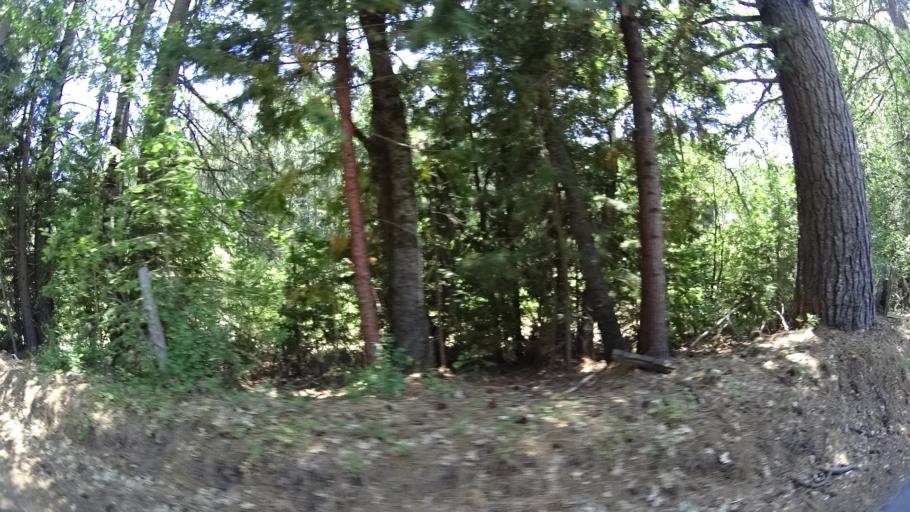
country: US
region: California
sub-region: Calaveras County
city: Arnold
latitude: 38.2344
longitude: -120.3220
